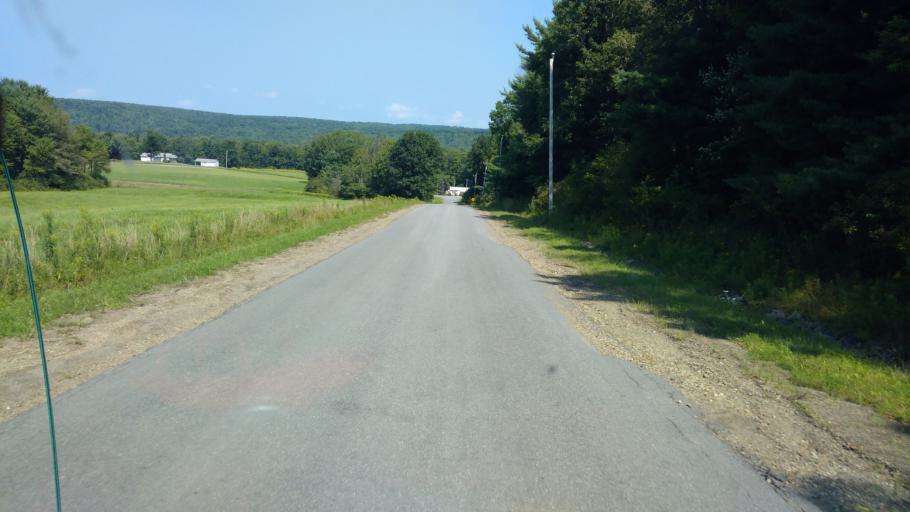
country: US
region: New York
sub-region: Allegany County
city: Houghton
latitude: 42.3391
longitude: -78.0741
